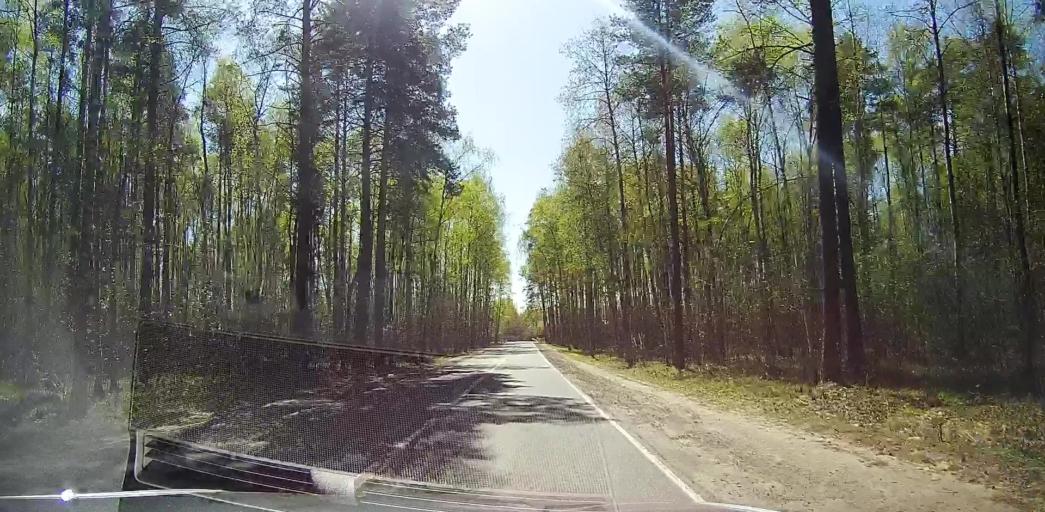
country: RU
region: Moskovskaya
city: Beloozerskiy
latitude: 55.4823
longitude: 38.4246
